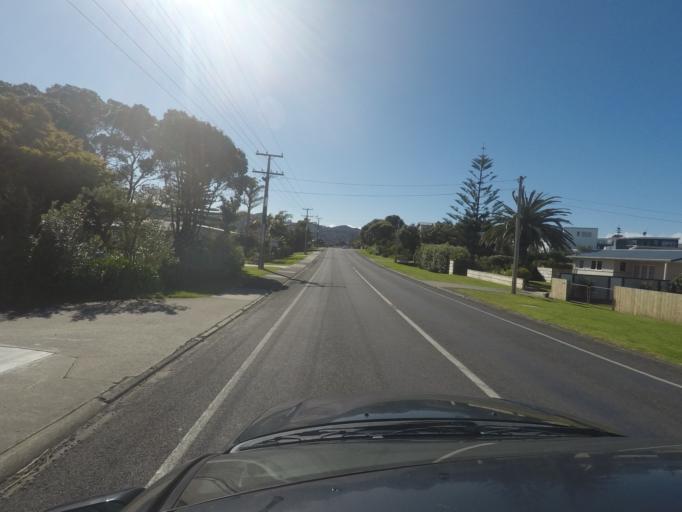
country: NZ
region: Bay of Plenty
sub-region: Western Bay of Plenty District
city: Waihi Beach
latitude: -37.4161
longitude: 175.9482
